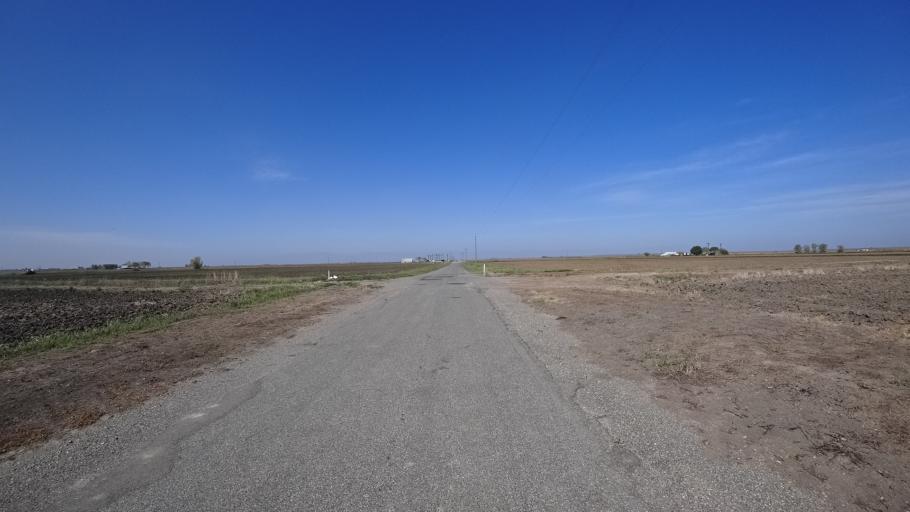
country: US
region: California
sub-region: Glenn County
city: Hamilton City
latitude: 39.6165
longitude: -122.0696
